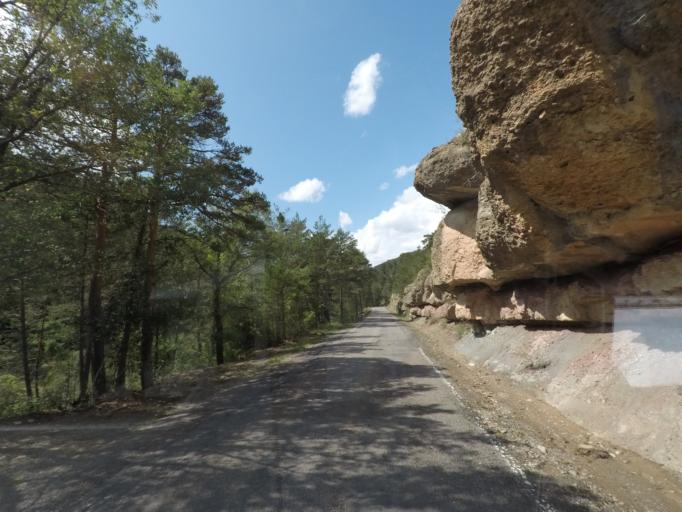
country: ES
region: Aragon
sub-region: Provincia de Huesca
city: Yebra de Basa
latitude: 42.4078
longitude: -0.2076
